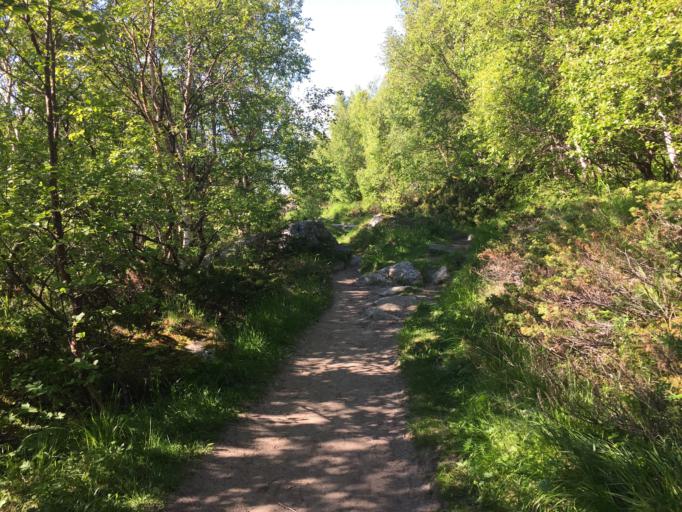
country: NO
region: Nordland
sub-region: Bodo
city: Loding
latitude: 67.4176
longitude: 14.6324
